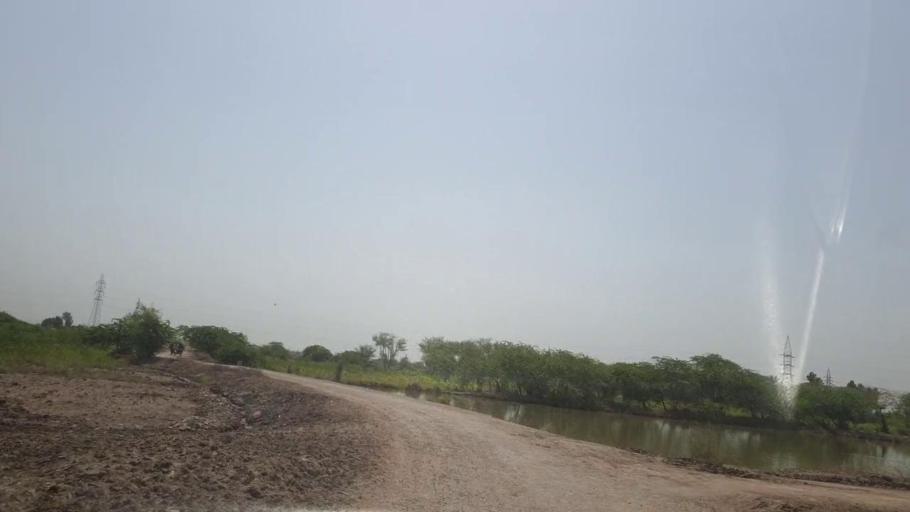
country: PK
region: Sindh
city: Gambat
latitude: 27.3163
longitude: 68.5349
